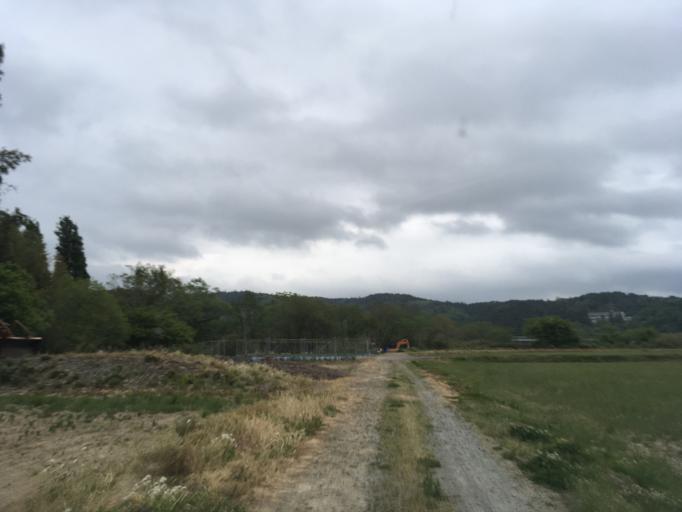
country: JP
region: Miyagi
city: Wakuya
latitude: 38.7182
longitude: 141.2910
